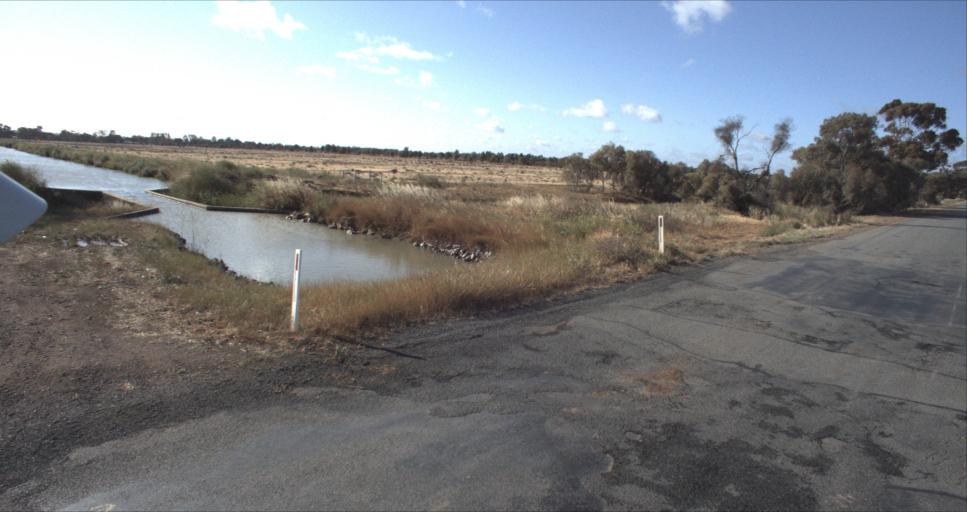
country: AU
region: New South Wales
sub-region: Leeton
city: Leeton
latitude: -34.5162
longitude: 146.3915
